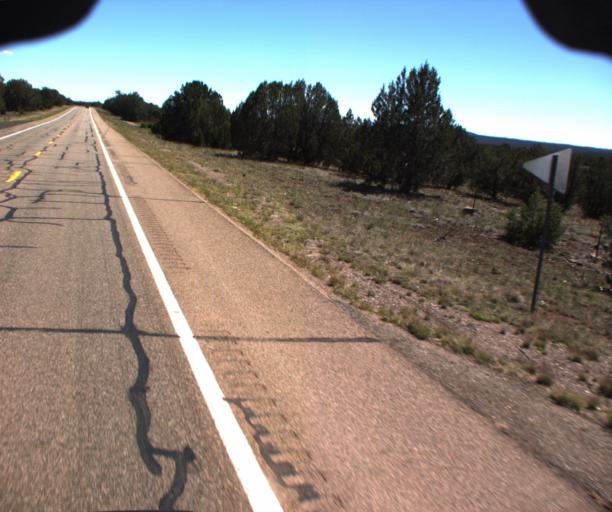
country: US
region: Arizona
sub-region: Yavapai County
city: Paulden
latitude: 35.1145
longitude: -112.4322
